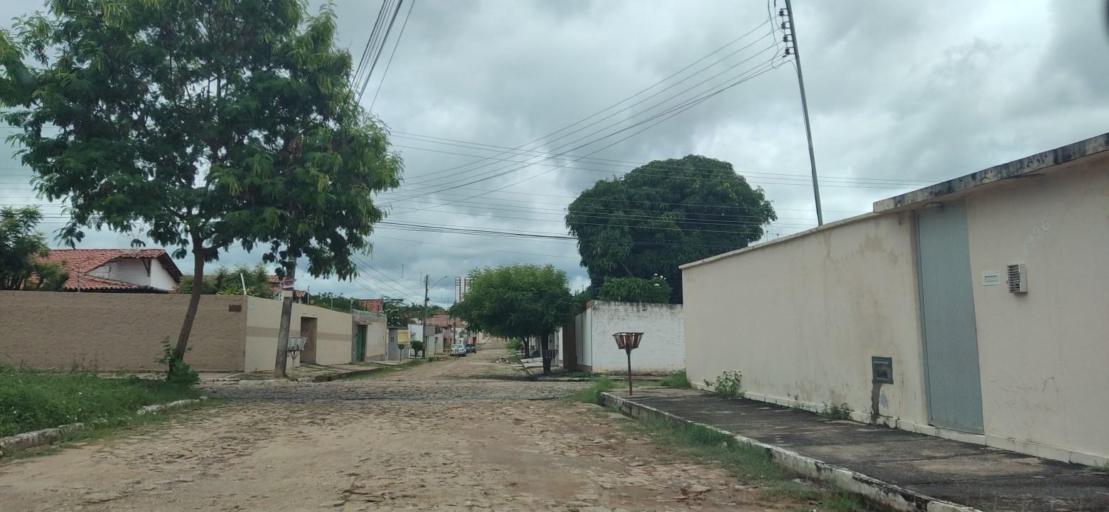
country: BR
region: Piaui
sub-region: Teresina
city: Teresina
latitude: -5.0710
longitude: -42.7579
